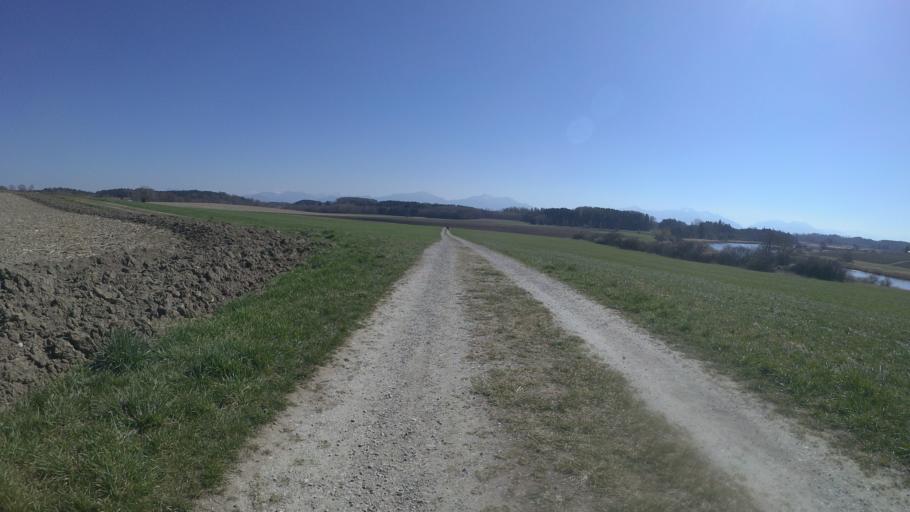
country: DE
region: Bavaria
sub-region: Upper Bavaria
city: Seeon-Seebruck
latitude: 47.9571
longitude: 12.4896
